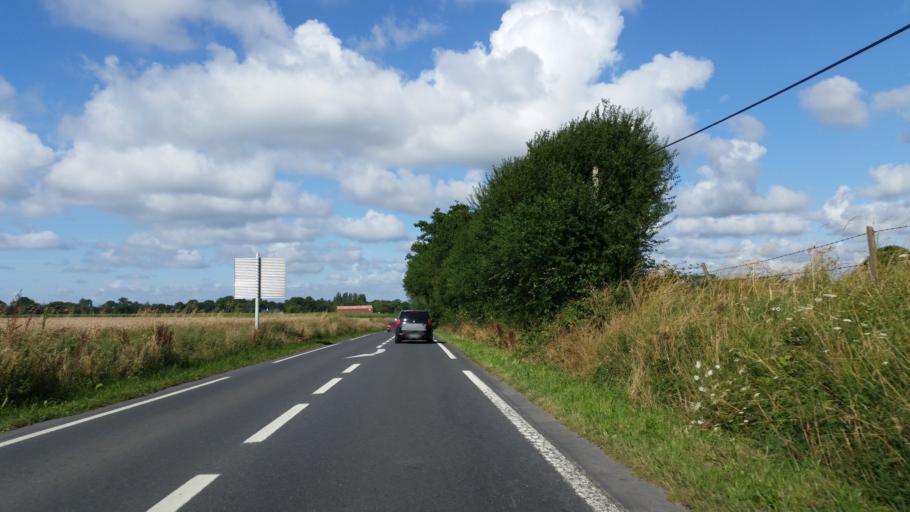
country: FR
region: Lower Normandy
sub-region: Departement du Calvados
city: Villers-sur-Mer
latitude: 49.2830
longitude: 0.0024
